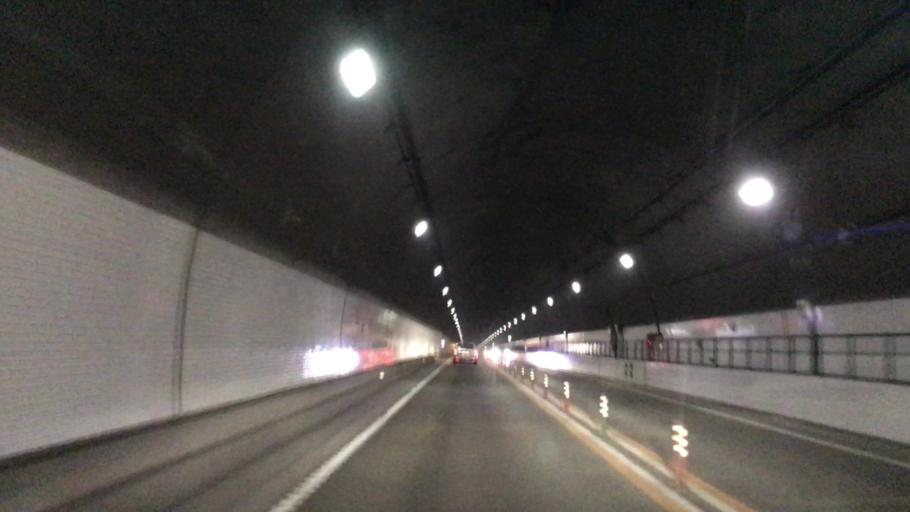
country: JP
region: Hokkaido
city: Shimo-furano
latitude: 42.9543
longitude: 142.2663
